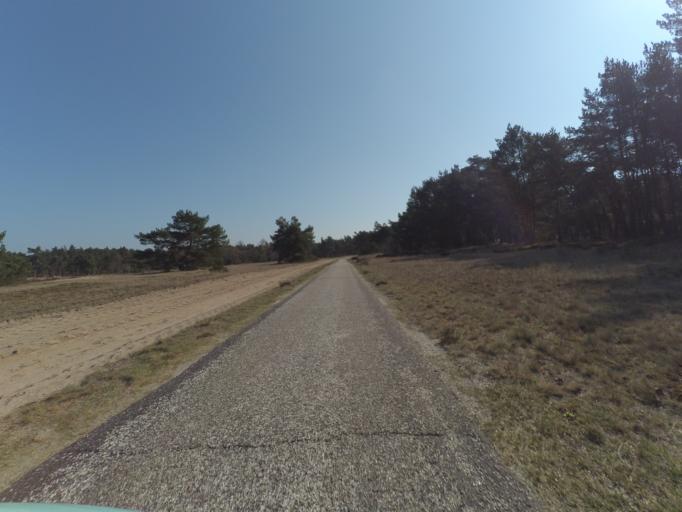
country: NL
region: Gelderland
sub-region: Gemeente Ede
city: Otterlo
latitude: 52.0699
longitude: 5.8429
